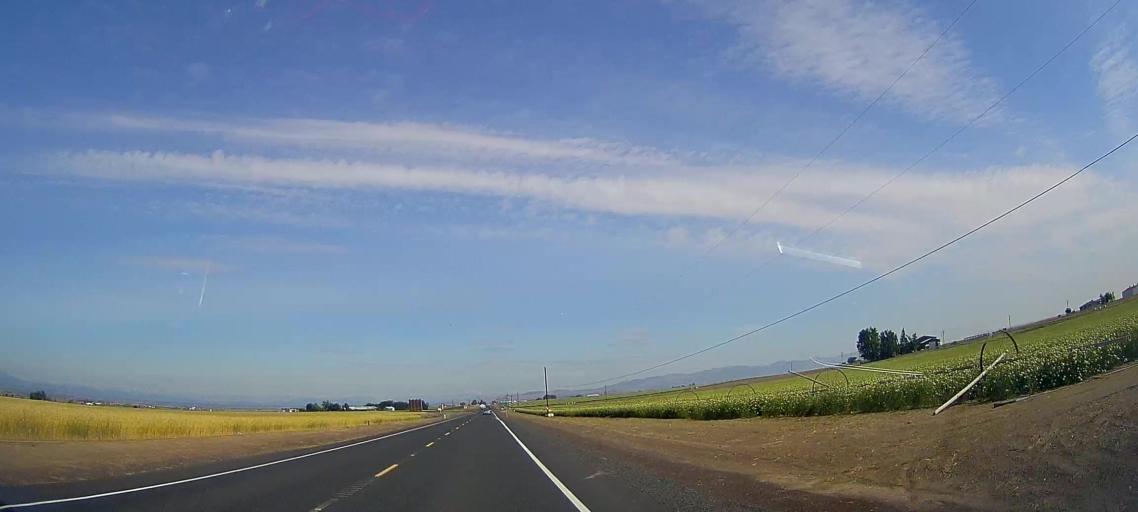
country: US
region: Oregon
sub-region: Jefferson County
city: Madras
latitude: 44.6757
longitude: -121.1438
